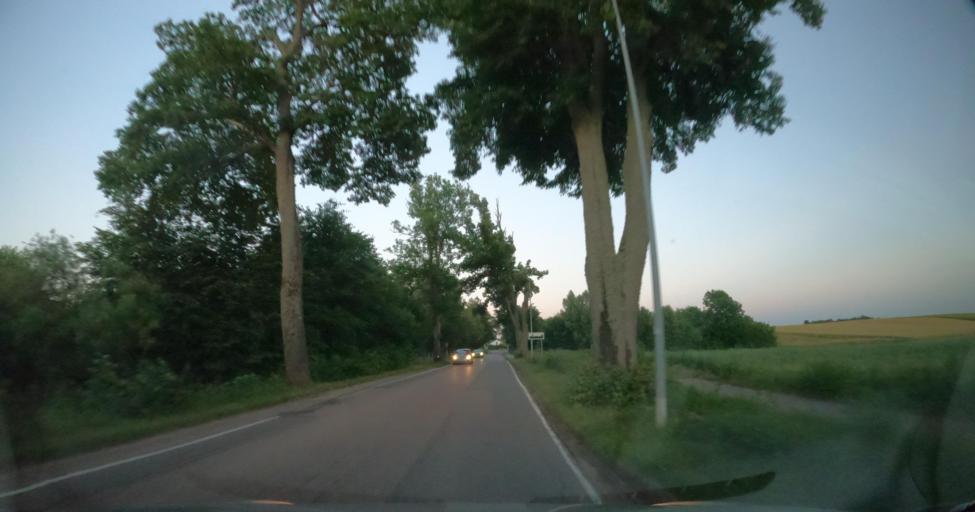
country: PL
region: Pomeranian Voivodeship
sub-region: Powiat wejherowski
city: Szemud
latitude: 54.4636
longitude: 18.1353
